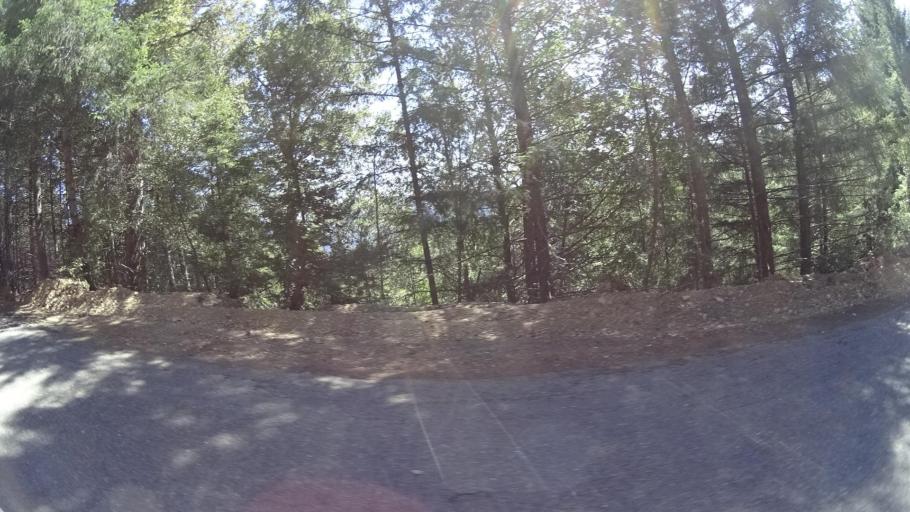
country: US
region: California
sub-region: Humboldt County
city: Redway
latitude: 40.1560
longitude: -124.0715
